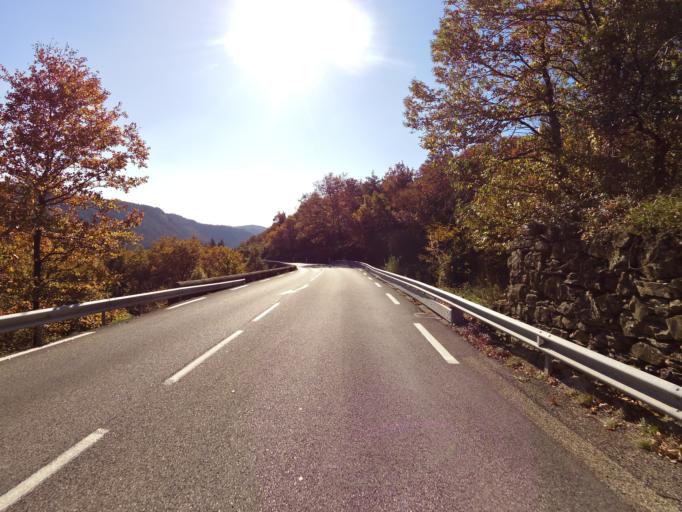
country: FR
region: Rhone-Alpes
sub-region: Departement de l'Ardeche
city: Vesseaux
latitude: 44.6818
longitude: 4.4613
